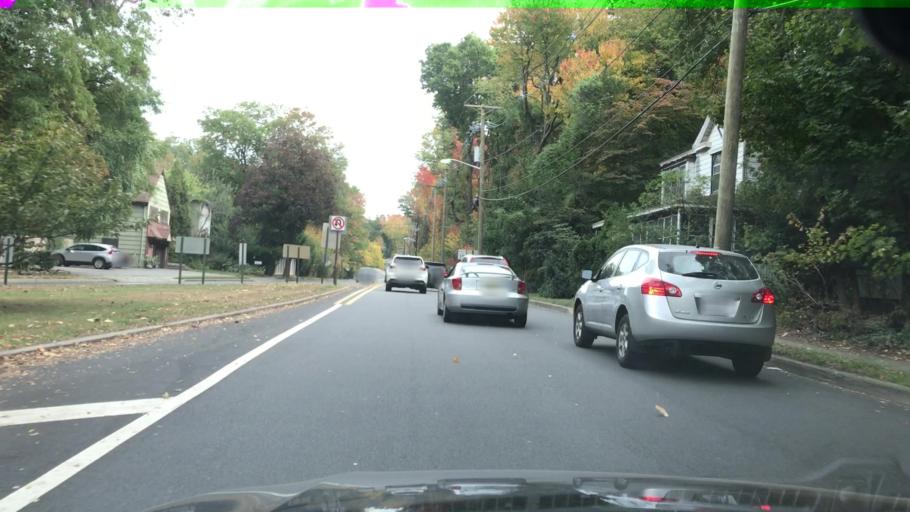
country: US
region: New Jersey
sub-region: Bergen County
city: Teaneck
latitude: 40.9158
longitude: -74.0237
